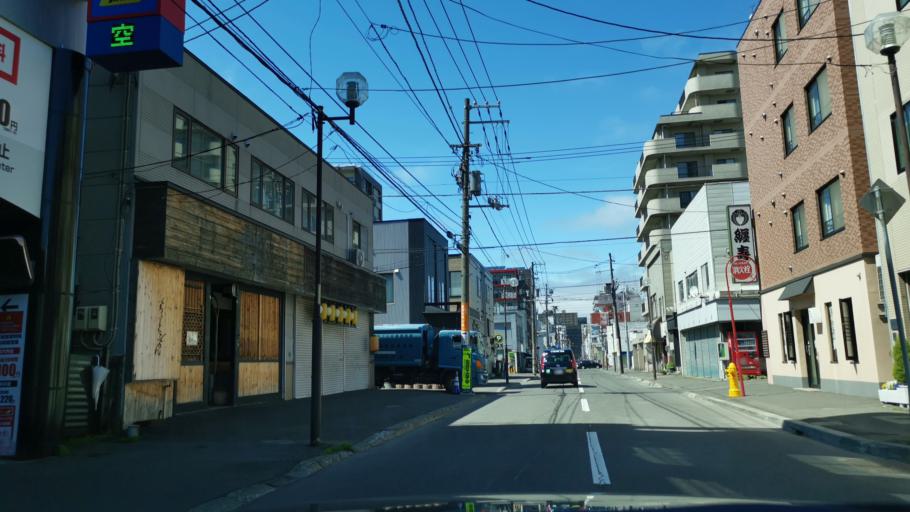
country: JP
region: Hokkaido
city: Sapporo
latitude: 43.0475
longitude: 141.3462
